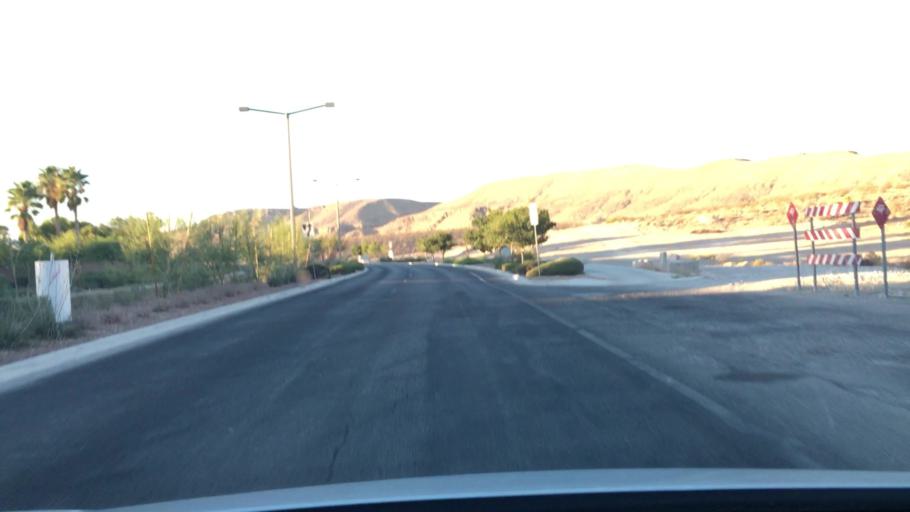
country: US
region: Nevada
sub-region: Clark County
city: Summerlin South
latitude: 36.1046
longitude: -115.3277
